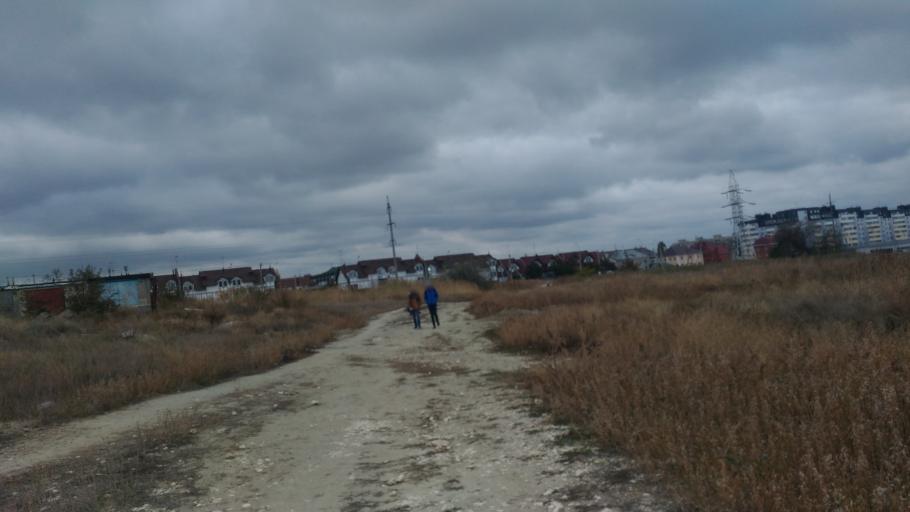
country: RU
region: Volgograd
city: Volgograd
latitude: 48.6433
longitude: 44.4240
